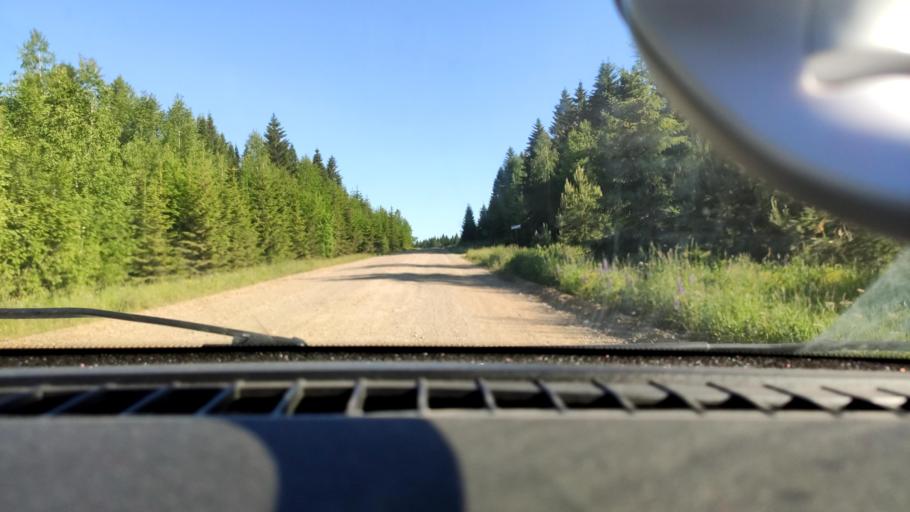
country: RU
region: Perm
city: Novyye Lyady
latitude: 58.1762
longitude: 56.5926
